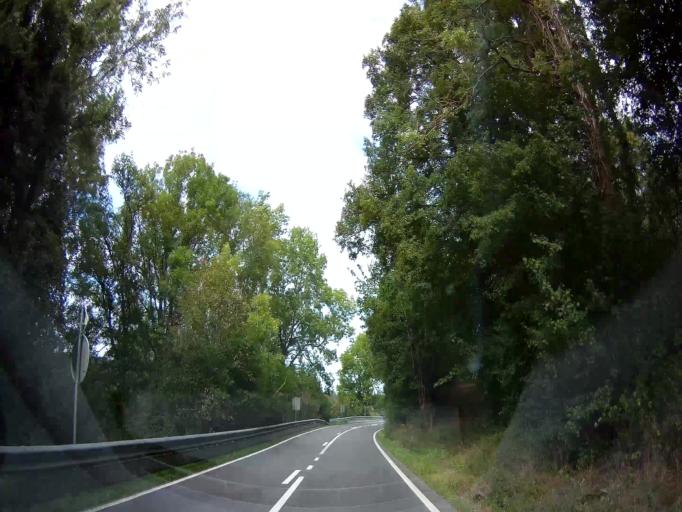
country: BE
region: Wallonia
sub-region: Province du Luxembourg
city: Durbuy
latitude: 50.3570
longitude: 5.5085
